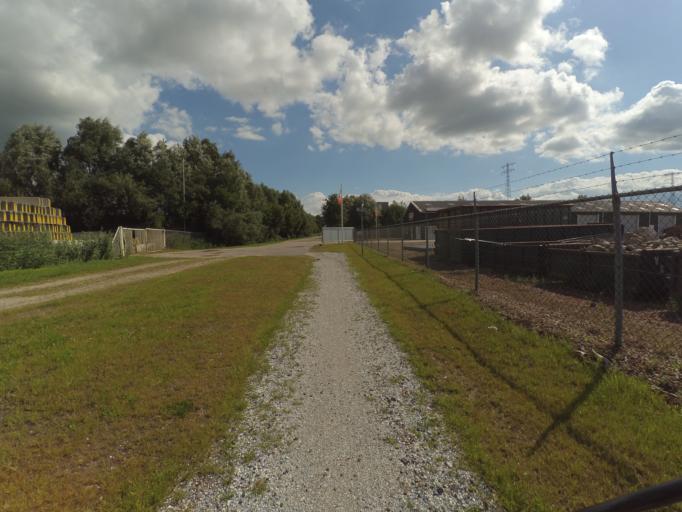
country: NL
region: Friesland
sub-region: Gemeente Achtkarspelen
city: Kootstertille
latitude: 53.2049
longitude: 6.0834
